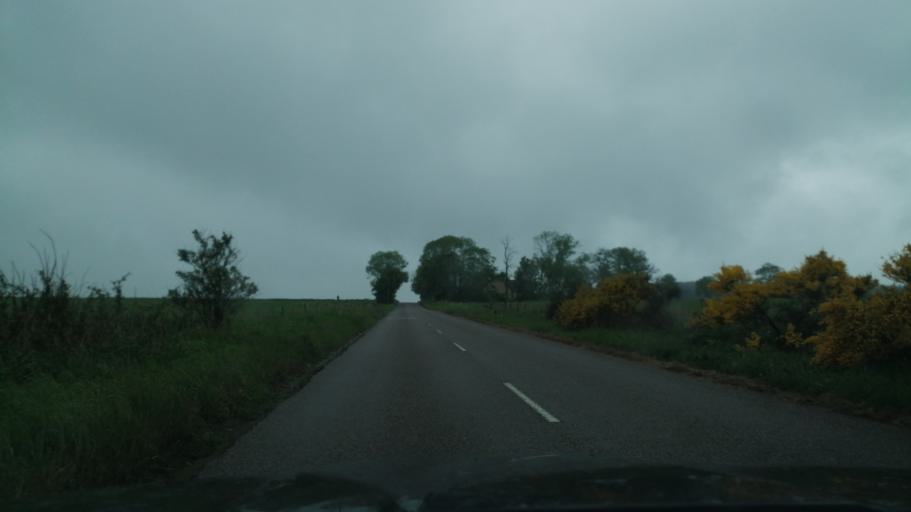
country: GB
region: Scotland
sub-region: Aberdeenshire
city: Huntly
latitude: 57.5455
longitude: -2.8110
